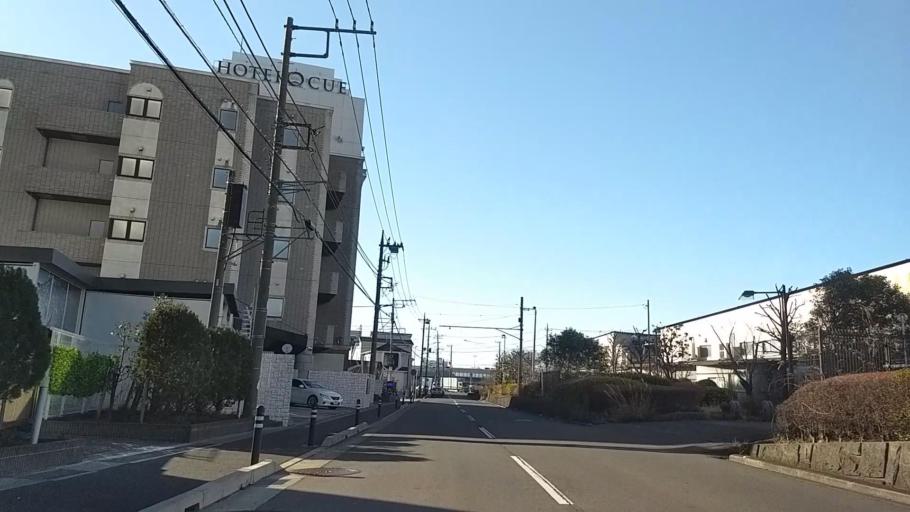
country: JP
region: Kanagawa
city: Atsugi
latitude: 35.4277
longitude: 139.3583
